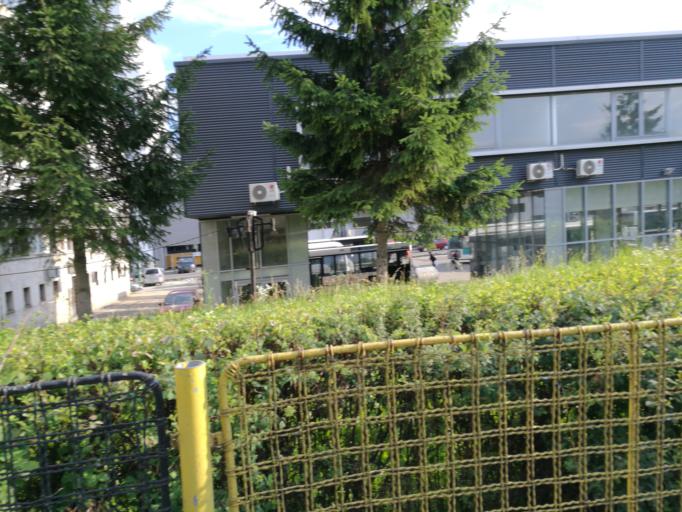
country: RO
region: Brasov
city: Brasov
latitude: 45.6612
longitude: 25.6147
